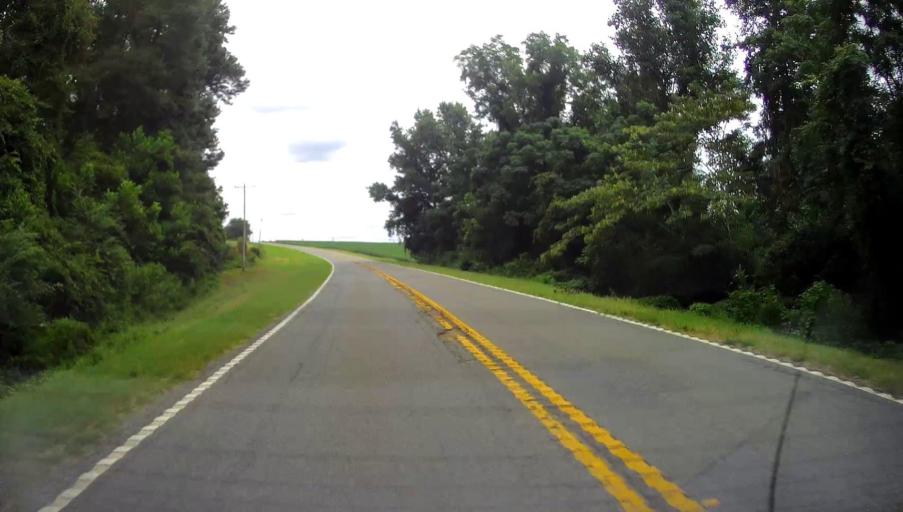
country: US
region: Georgia
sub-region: Dooly County
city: Unadilla
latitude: 32.2591
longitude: -83.8015
